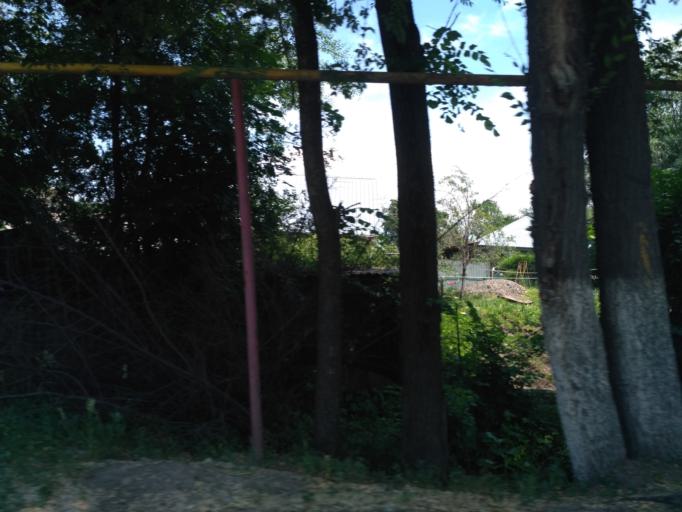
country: KZ
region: Almaty Oblysy
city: Burunday
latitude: 43.1883
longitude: 76.6200
